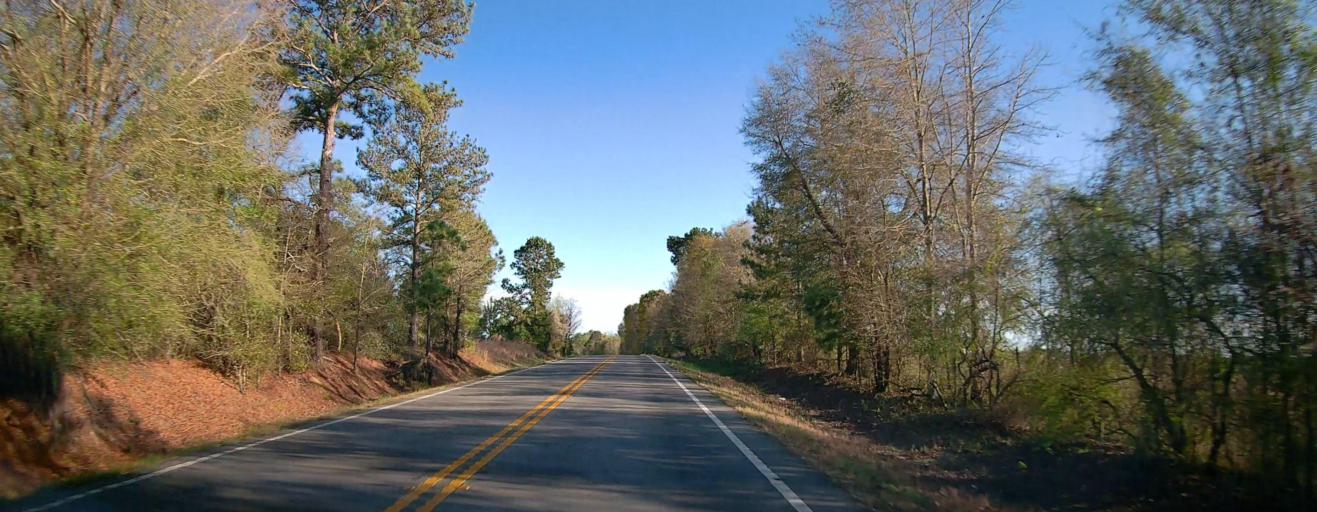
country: US
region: Georgia
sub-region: Pulaski County
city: Hawkinsville
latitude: 32.2335
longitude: -83.3976
